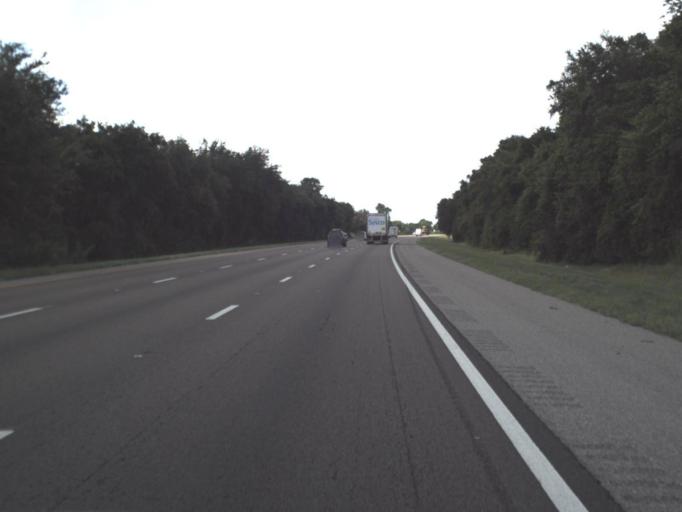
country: US
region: Florida
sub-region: Hillsborough County
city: Apollo Beach
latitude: 27.7696
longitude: -82.3645
